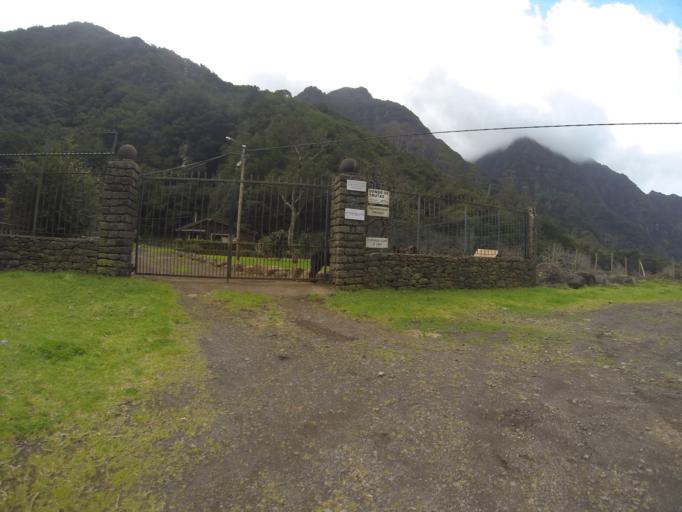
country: PT
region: Madeira
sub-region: Sao Vicente
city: Sao Vicente
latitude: 32.7967
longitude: -17.1140
